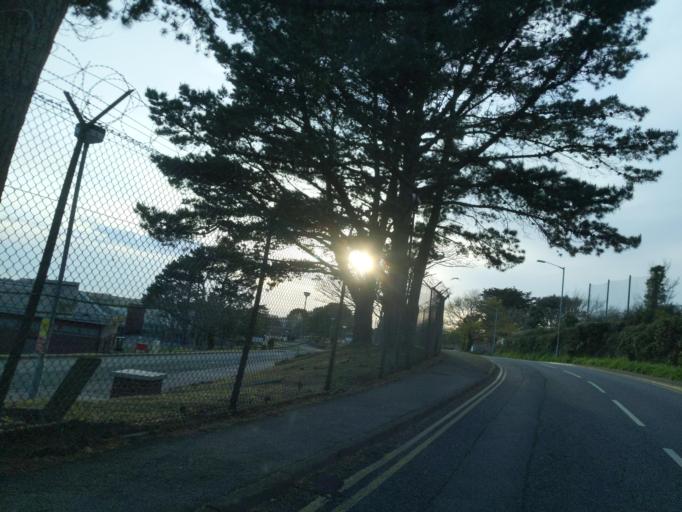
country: GB
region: England
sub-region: Cornwall
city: Torpoint
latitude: 50.3742
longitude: -4.2193
